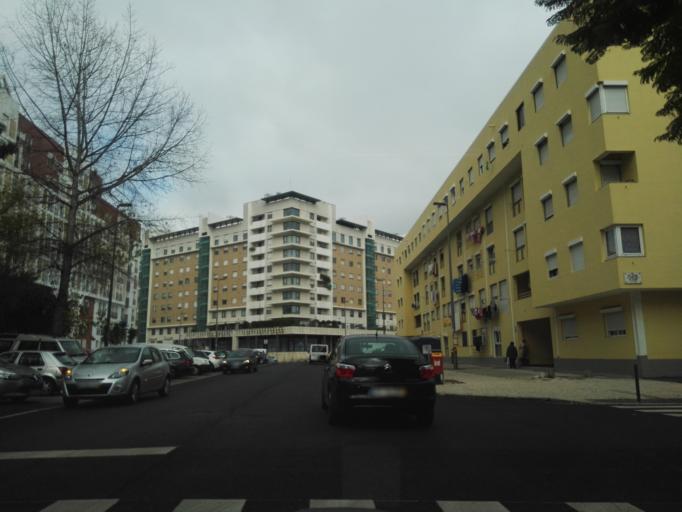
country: PT
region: Lisbon
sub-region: Odivelas
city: Pontinha
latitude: 38.7540
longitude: -9.1689
